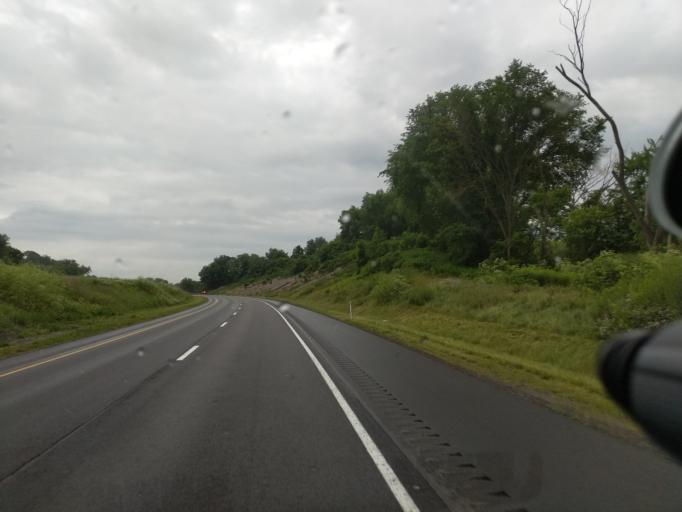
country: US
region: Pennsylvania
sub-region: Northumberland County
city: Milton
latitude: 41.0416
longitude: -76.8126
